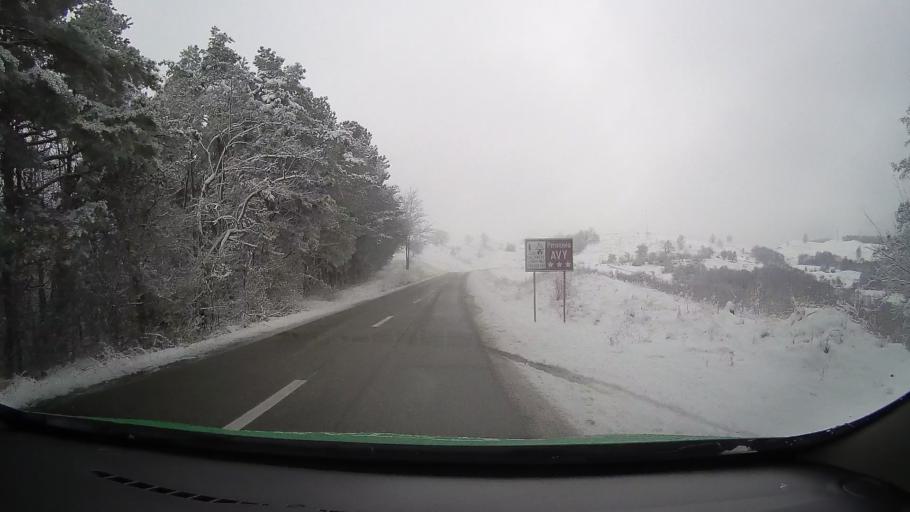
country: RO
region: Hunedoara
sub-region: Comuna Teliucu Inferior
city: Teliucu Inferior
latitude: 45.6695
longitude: 22.9177
